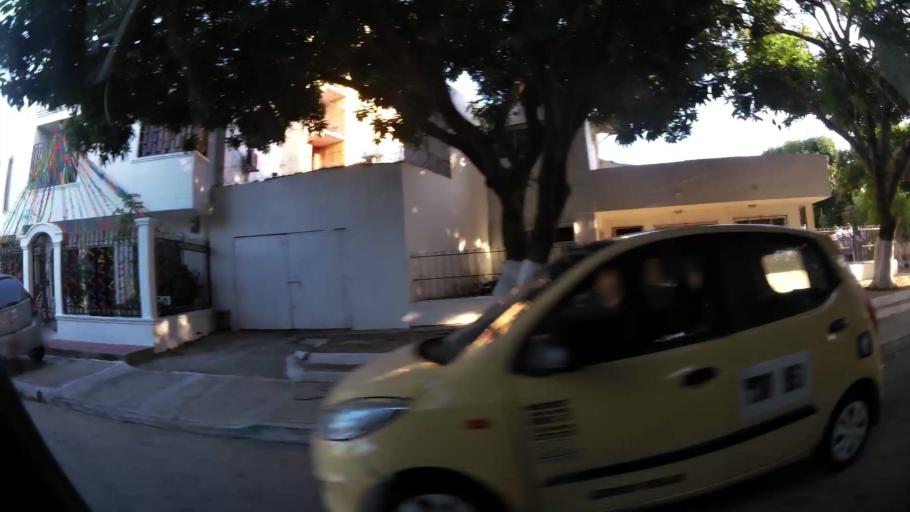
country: CO
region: Atlantico
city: Barranquilla
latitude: 10.9646
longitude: -74.7945
